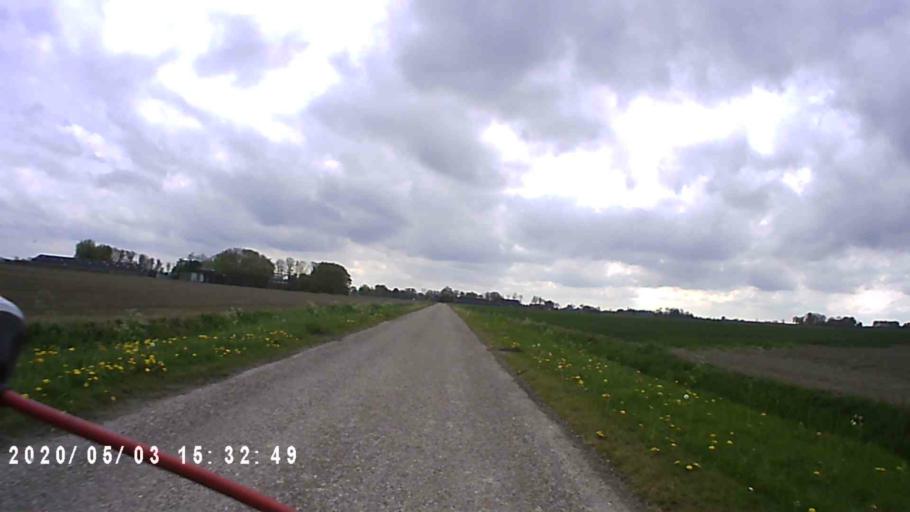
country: NL
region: Groningen
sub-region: Gemeente Winsum
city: Winsum
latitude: 53.3384
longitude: 6.4735
